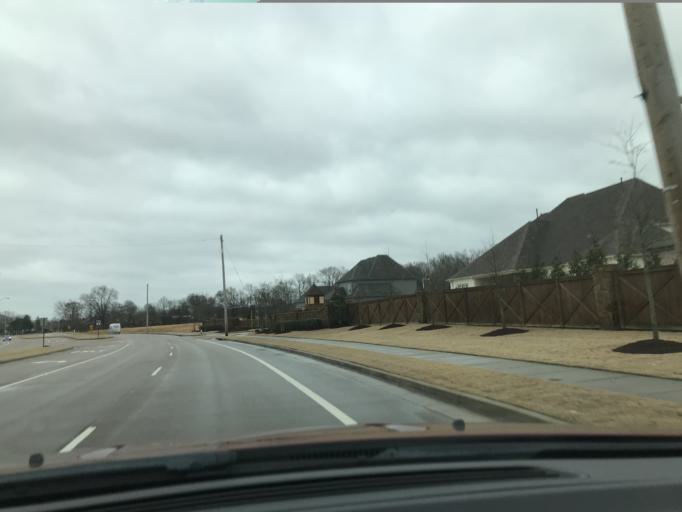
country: US
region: Tennessee
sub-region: Shelby County
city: Collierville
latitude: 35.0869
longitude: -89.7053
